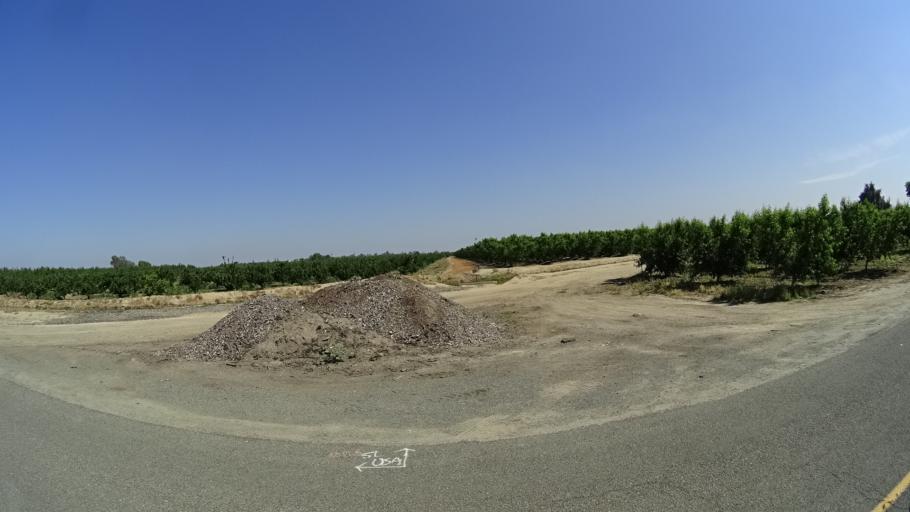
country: US
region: California
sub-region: Fresno County
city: Kingsburg
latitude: 36.4668
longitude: -119.5577
